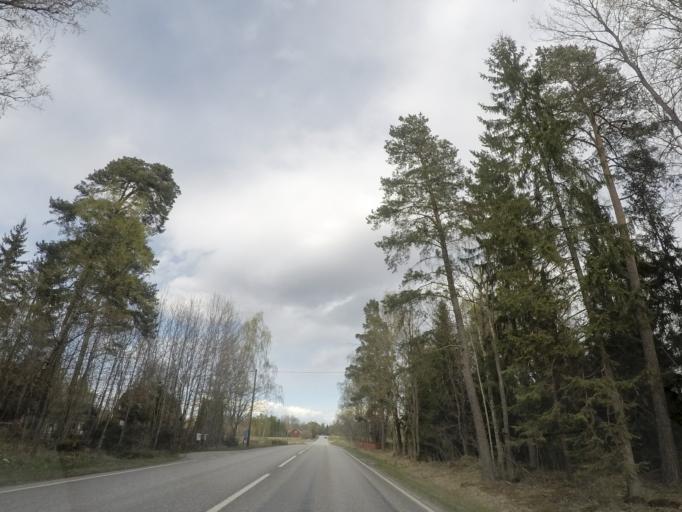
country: SE
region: Soedermanland
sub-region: Eskilstuna Kommun
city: Kvicksund
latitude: 59.3114
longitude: 16.2648
